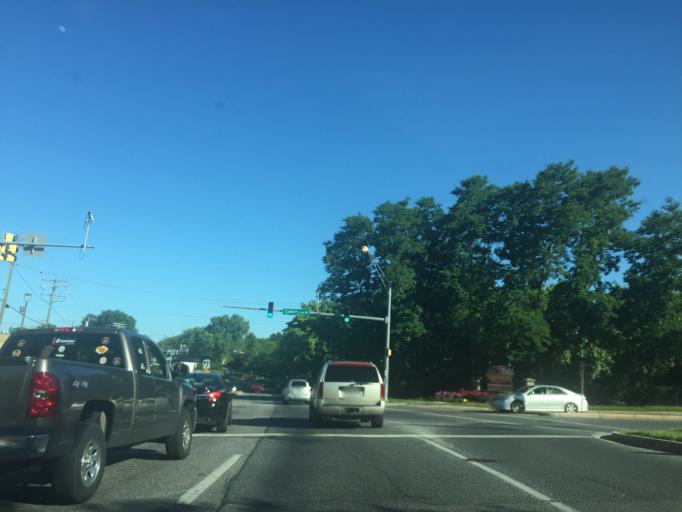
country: US
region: Maryland
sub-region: Baltimore County
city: Towson
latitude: 39.3850
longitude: -76.5802
